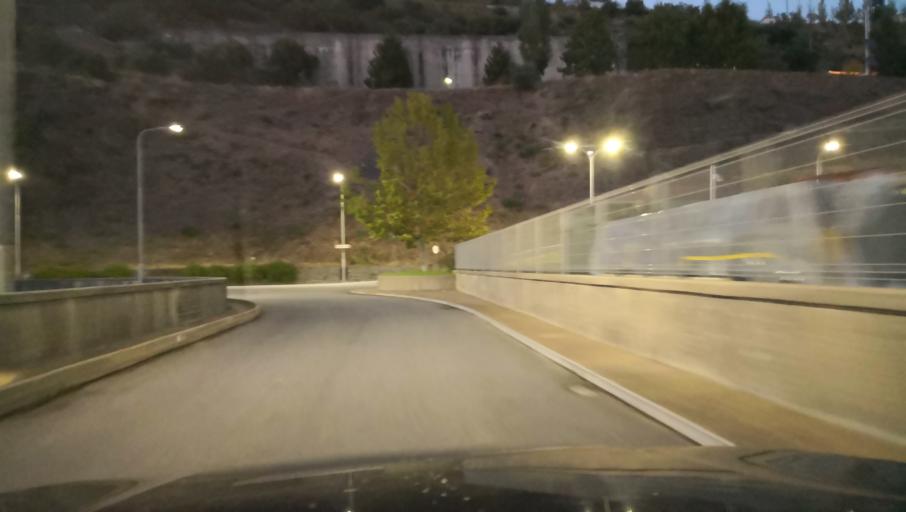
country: PT
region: Vila Real
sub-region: Peso da Regua
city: Peso da Regua
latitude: 41.1476
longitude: -7.7395
